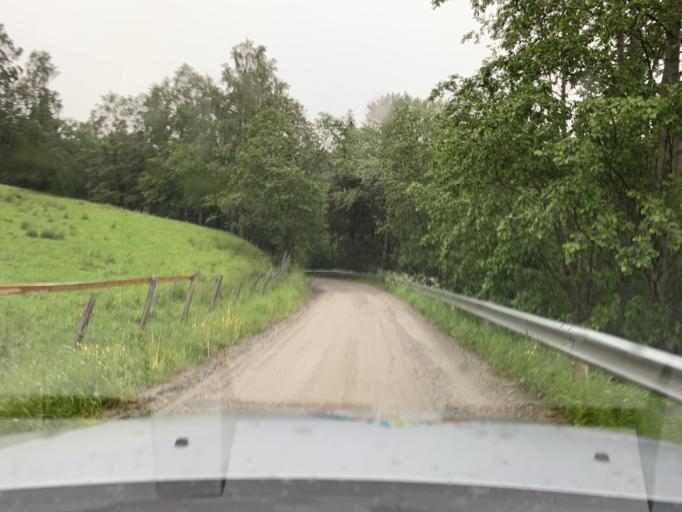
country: NO
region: Oppland
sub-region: Oyer
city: Tretten
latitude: 61.3900
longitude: 10.2696
